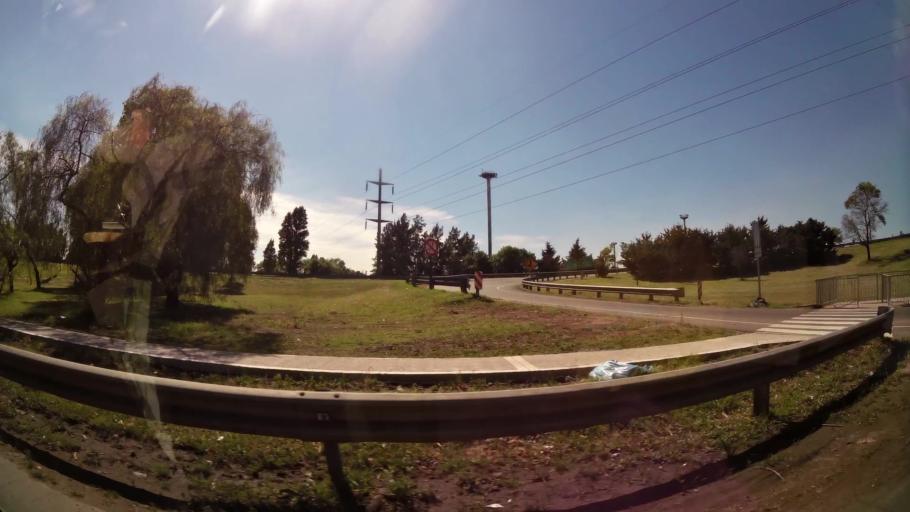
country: AR
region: Buenos Aires
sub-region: Partido de San Isidro
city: San Isidro
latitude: -34.4931
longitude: -58.5582
